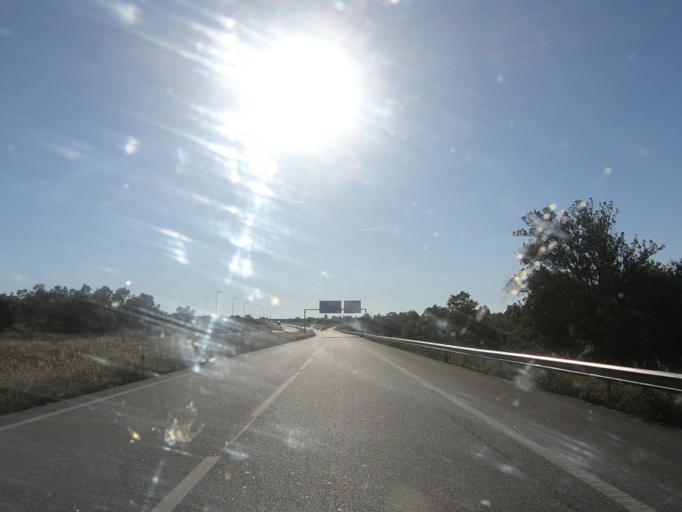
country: ES
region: Castille and Leon
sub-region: Provincia de Salamanca
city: Fuentes de Onoro
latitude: 40.6061
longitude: -6.9752
